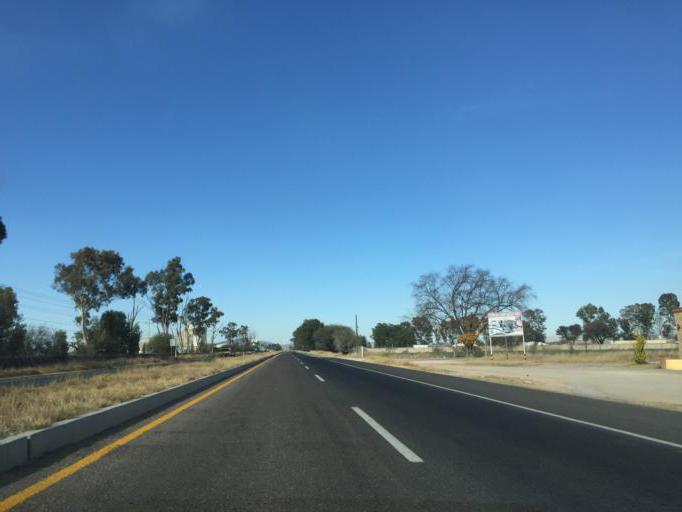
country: MX
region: Queretaro
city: Ezequiel Montes
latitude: 20.6242
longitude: -99.9124
